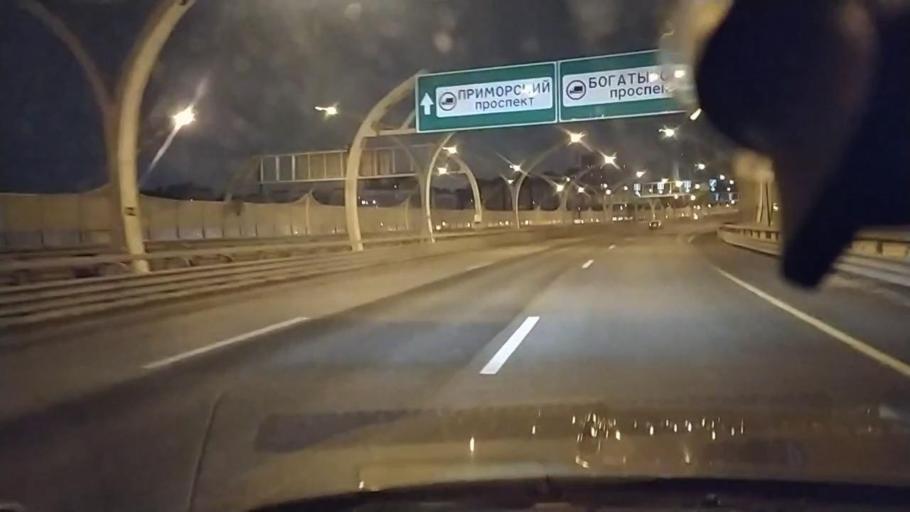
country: RU
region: St.-Petersburg
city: Staraya Derevnya
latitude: 60.0094
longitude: 30.2332
